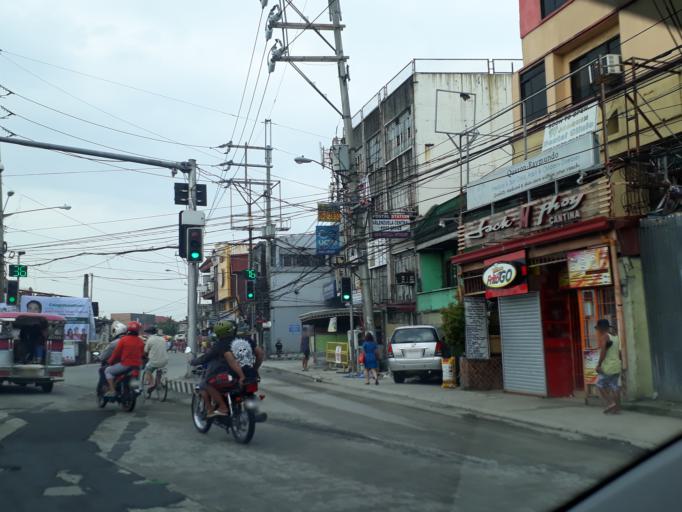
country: PH
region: Central Luzon
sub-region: Province of Bulacan
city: Meycauayan
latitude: 14.7185
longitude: 120.9573
